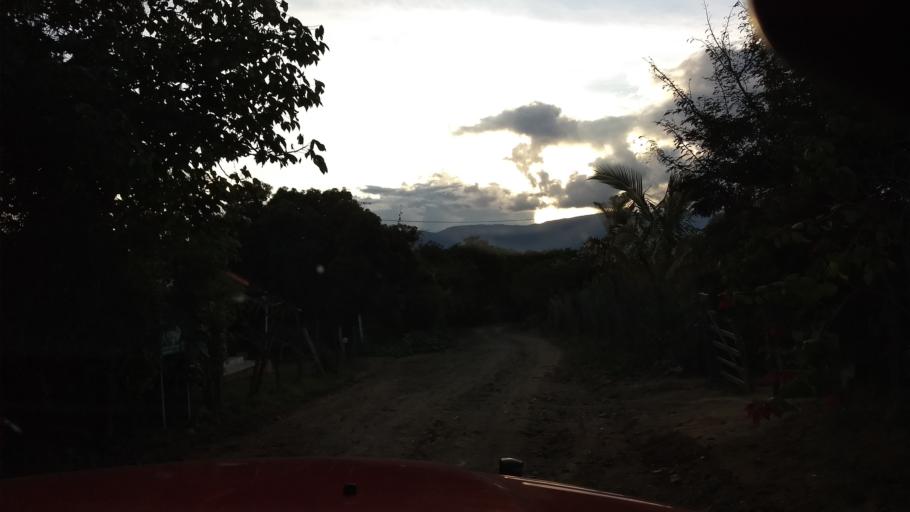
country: MX
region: Colima
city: Suchitlan
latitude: 19.4971
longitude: -103.7709
